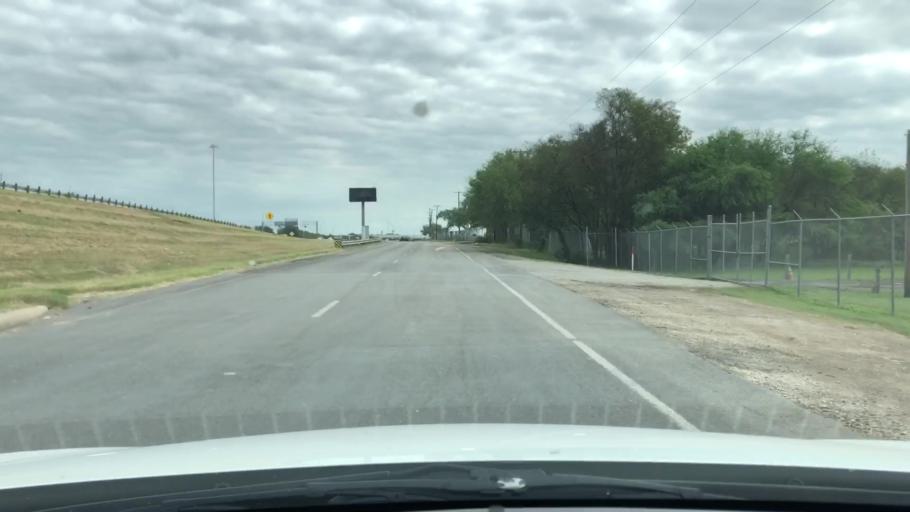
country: US
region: Texas
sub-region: Bexar County
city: Lackland Air Force Base
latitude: 29.4070
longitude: -98.5995
